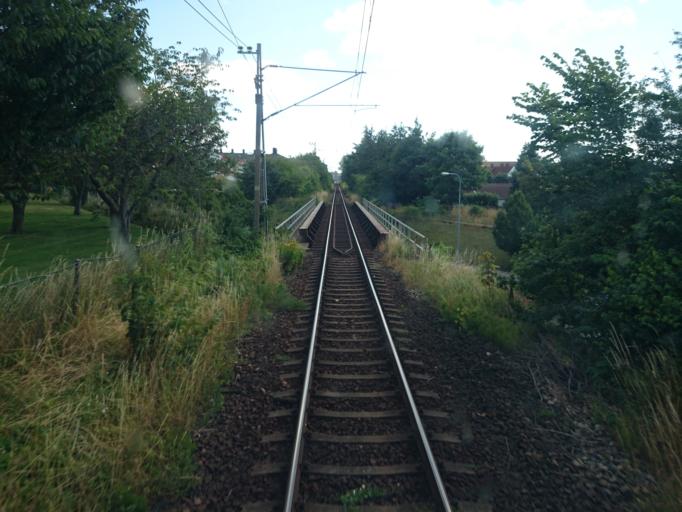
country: SE
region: Skane
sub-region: Ystads Kommun
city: Ystad
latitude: 55.4263
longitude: 13.8030
